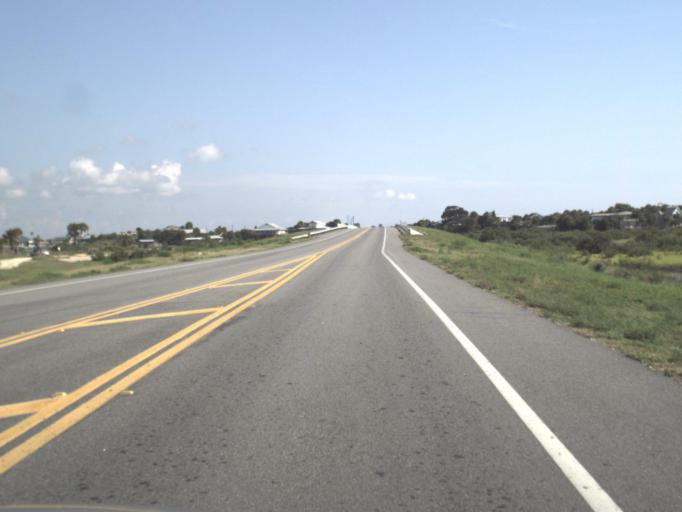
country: US
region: Florida
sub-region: Flagler County
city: Palm Coast
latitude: 29.6937
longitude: -81.2245
